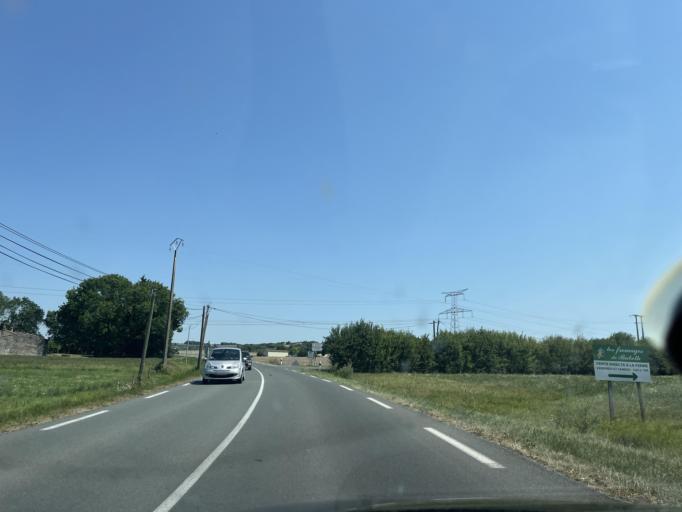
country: FR
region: Poitou-Charentes
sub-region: Departement de la Charente-Maritime
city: Mirambeau
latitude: 45.4189
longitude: -0.6324
